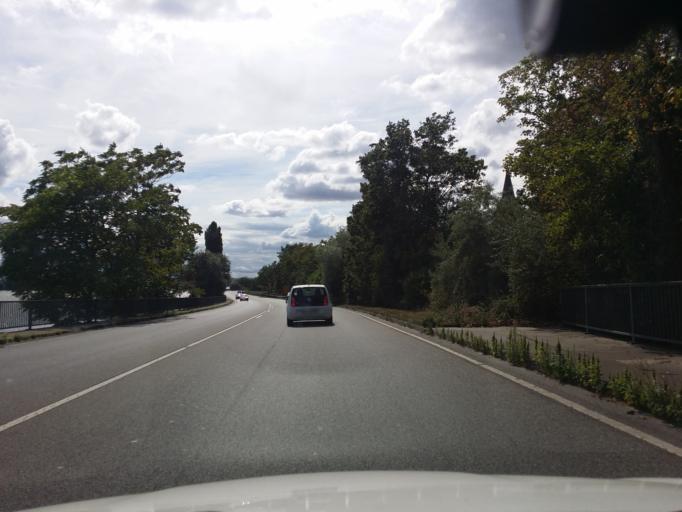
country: DE
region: Rheinland-Pfalz
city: Oestrich-Winkel
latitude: 50.0054
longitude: 8.0342
